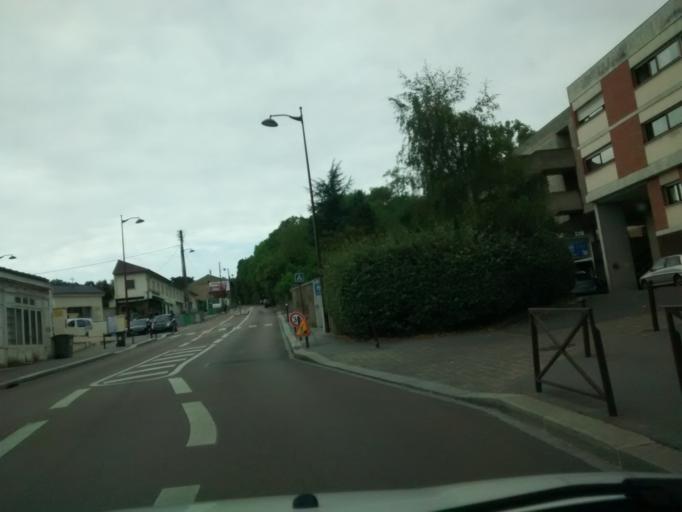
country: FR
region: Ile-de-France
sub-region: Departement des Yvelines
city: Versailles
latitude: 48.7941
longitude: 2.1376
